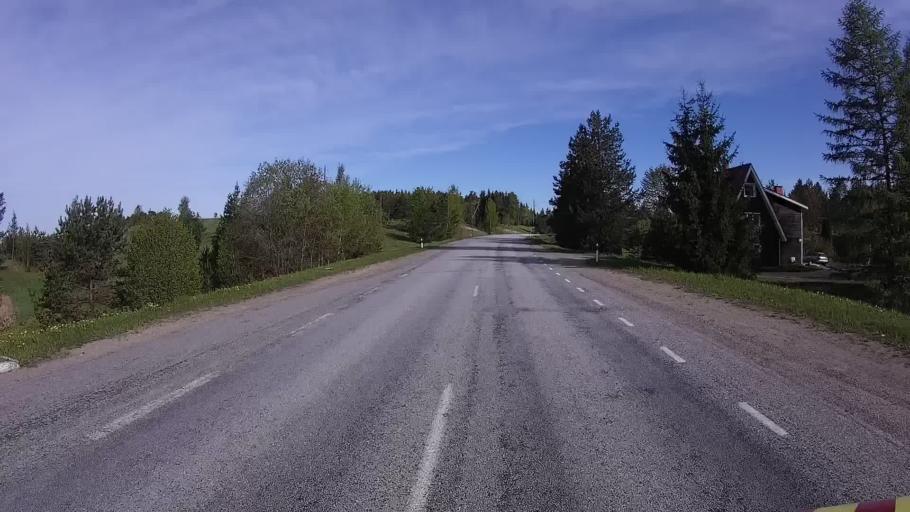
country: EE
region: Tartu
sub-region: Elva linn
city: Elva
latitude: 58.0843
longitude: 26.4927
